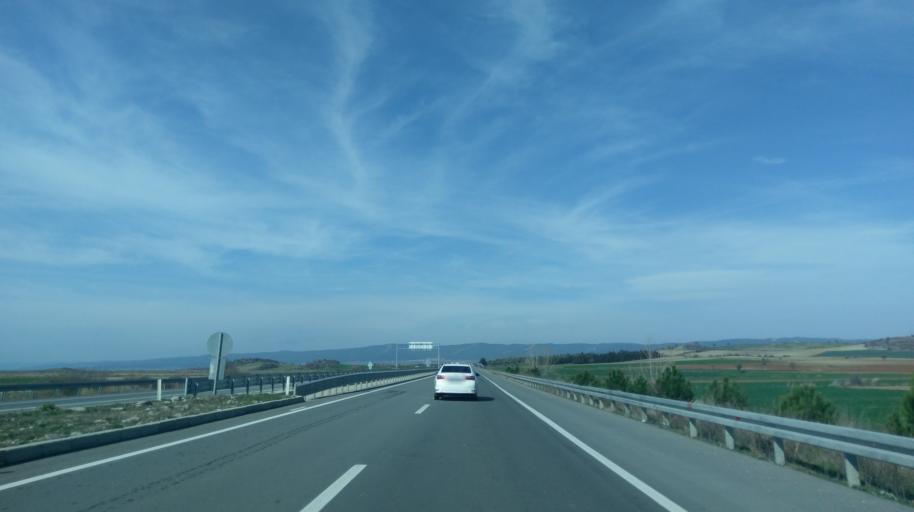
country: TR
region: Canakkale
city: Evrese
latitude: 40.6407
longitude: 26.8563
